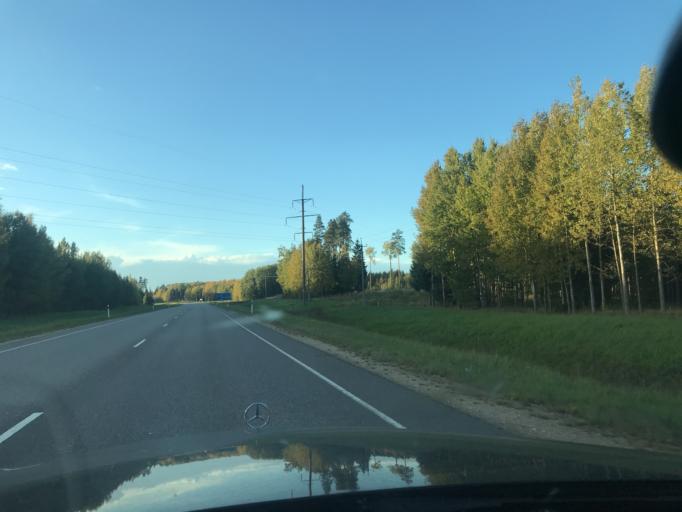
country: EE
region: Vorumaa
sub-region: Voru linn
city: Voru
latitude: 57.8456
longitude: 27.0448
